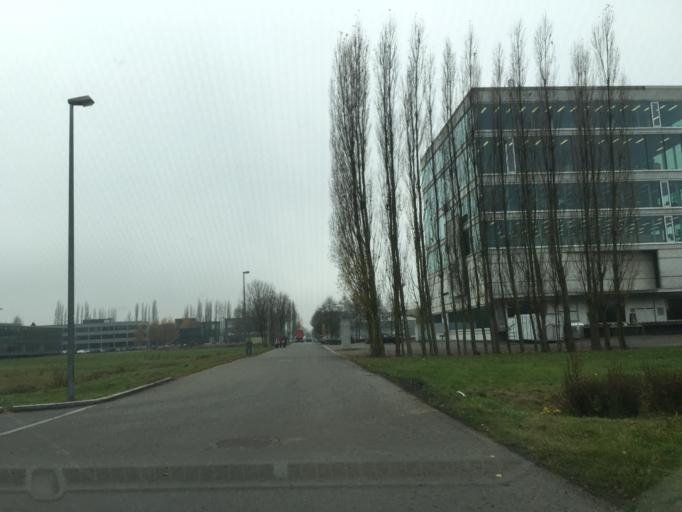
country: AT
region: Vorarlberg
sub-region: Politischer Bezirk Dornbirn
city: Lustenau
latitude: 47.4228
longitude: 9.6716
